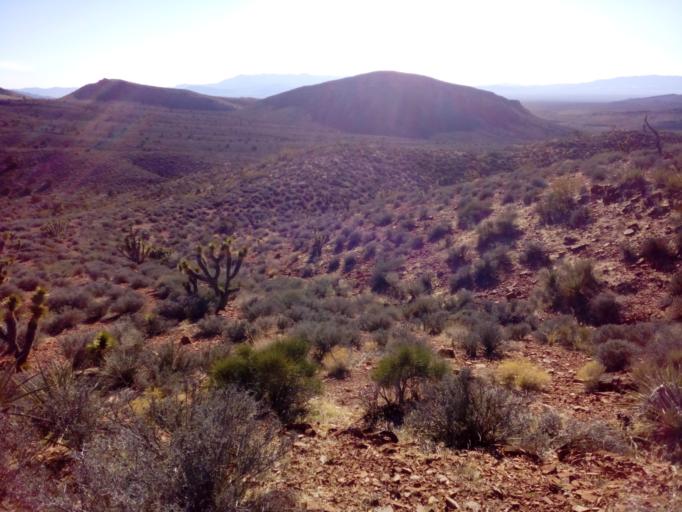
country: US
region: Nevada
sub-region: Clark County
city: Sandy Valley
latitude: 36.0647
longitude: -115.5802
